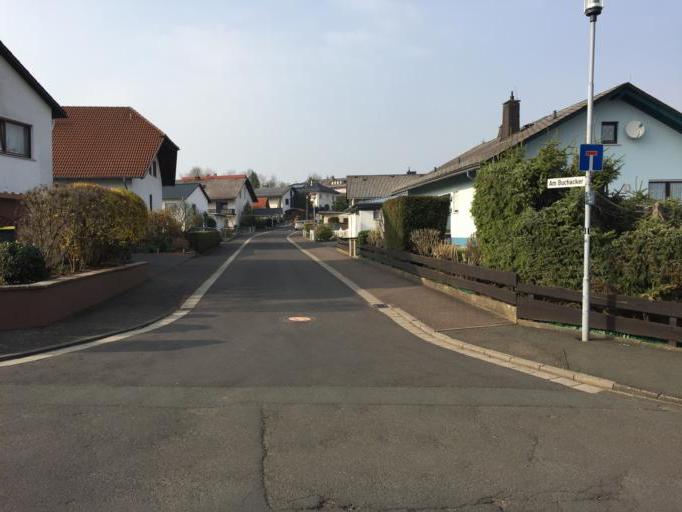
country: DE
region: Hesse
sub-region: Regierungsbezirk Giessen
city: Wetzlar
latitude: 50.6407
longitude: 8.5331
